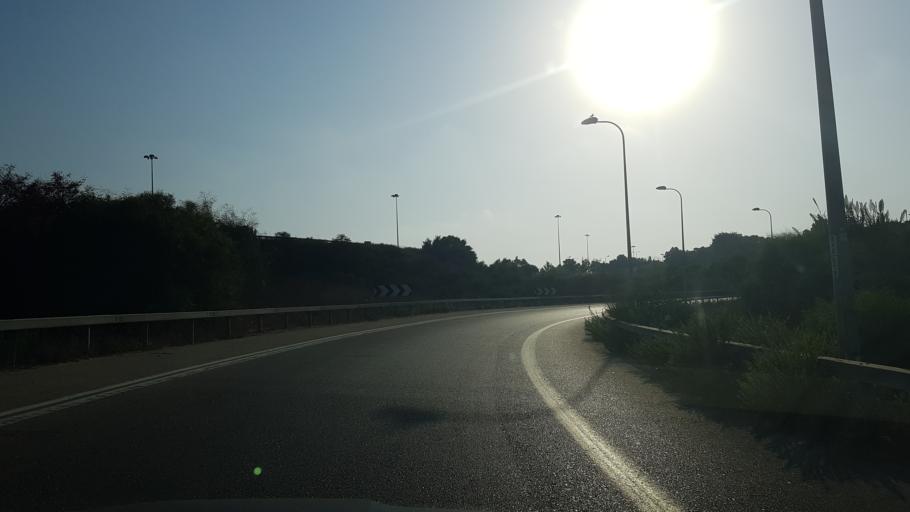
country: IL
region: Tel Aviv
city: Herzliyya
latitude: 32.1424
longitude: 34.8084
